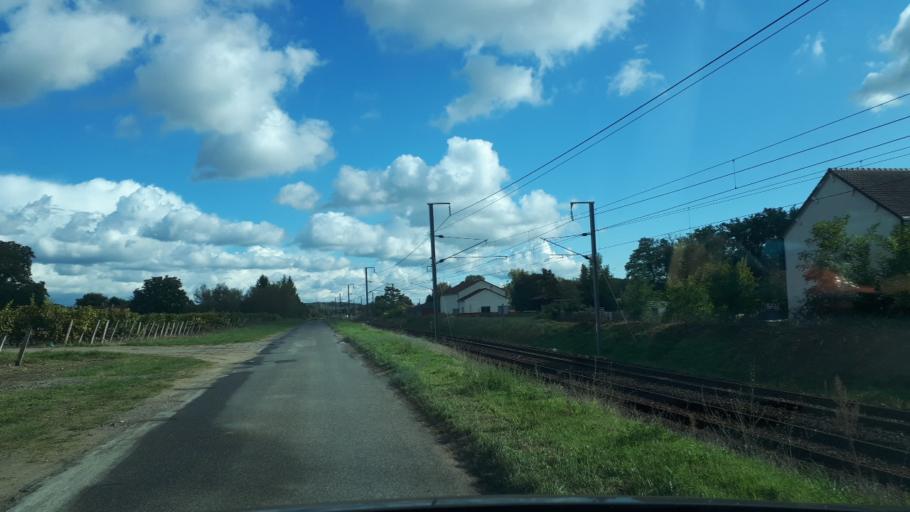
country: FR
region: Centre
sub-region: Departement du Loir-et-Cher
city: Thesee
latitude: 47.3176
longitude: 1.3251
